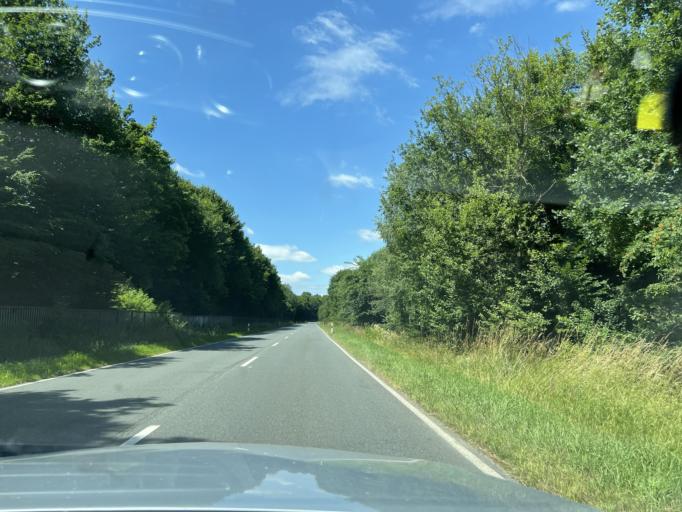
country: DE
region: North Rhine-Westphalia
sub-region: Regierungsbezirk Arnsberg
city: Wenden
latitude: 50.9676
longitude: 7.8976
